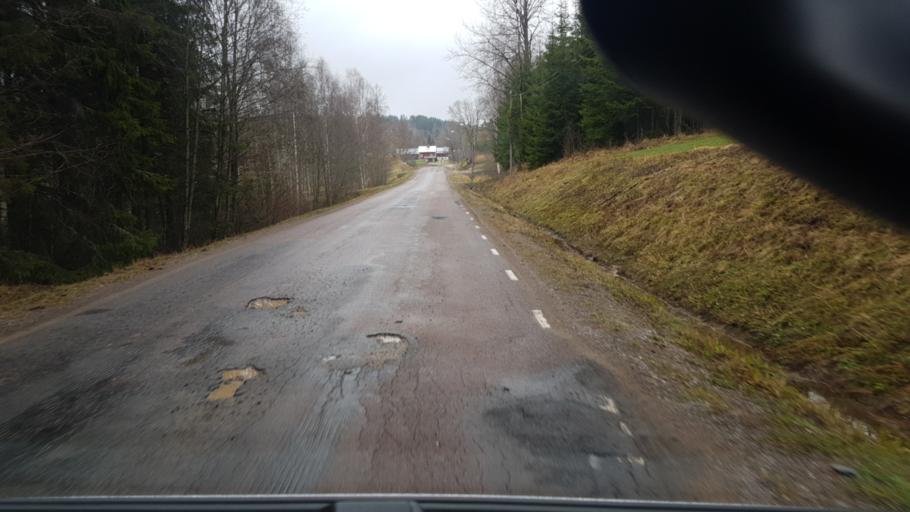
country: SE
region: Vaermland
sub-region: Eda Kommun
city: Charlottenberg
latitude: 59.9274
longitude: 12.5210
